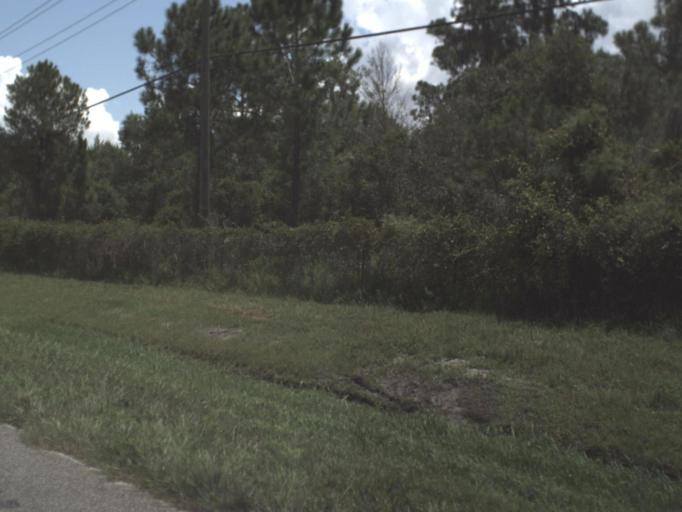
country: US
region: Florida
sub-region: Hillsborough County
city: Sun City Center
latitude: 27.6662
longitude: -82.3594
